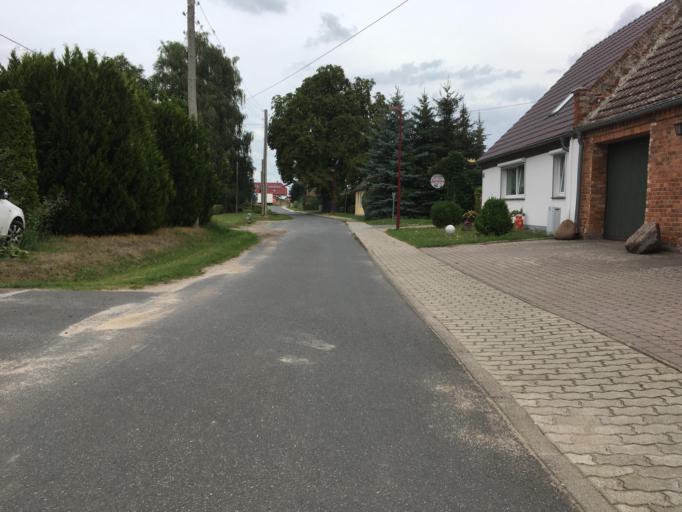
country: DE
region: Brandenburg
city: Prenzlau
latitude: 53.2778
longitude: 13.8440
